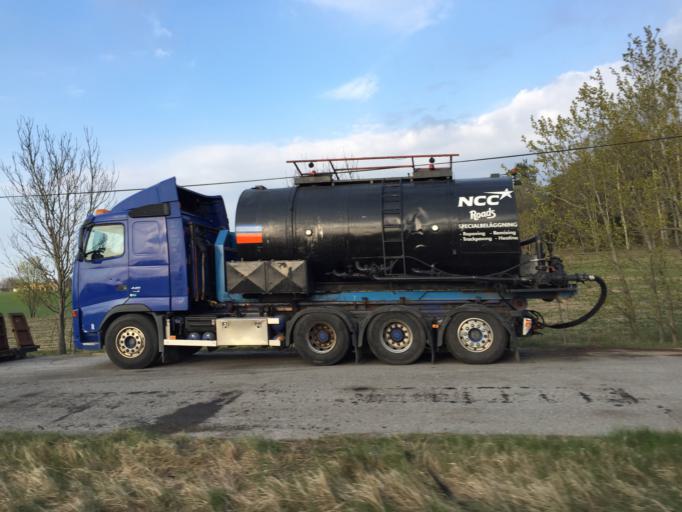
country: SE
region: Stockholm
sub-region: Sodertalje Kommun
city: Pershagen
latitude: 59.0590
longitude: 17.6133
